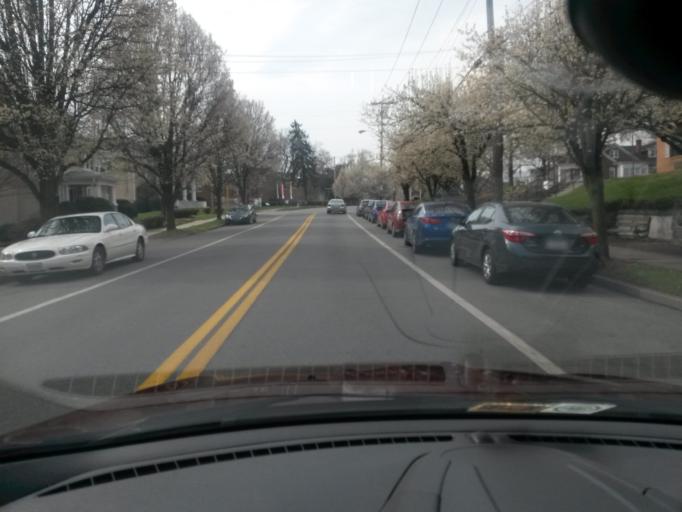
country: US
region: Virginia
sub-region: City of Roanoke
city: Roanoke
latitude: 37.2627
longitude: -79.9782
